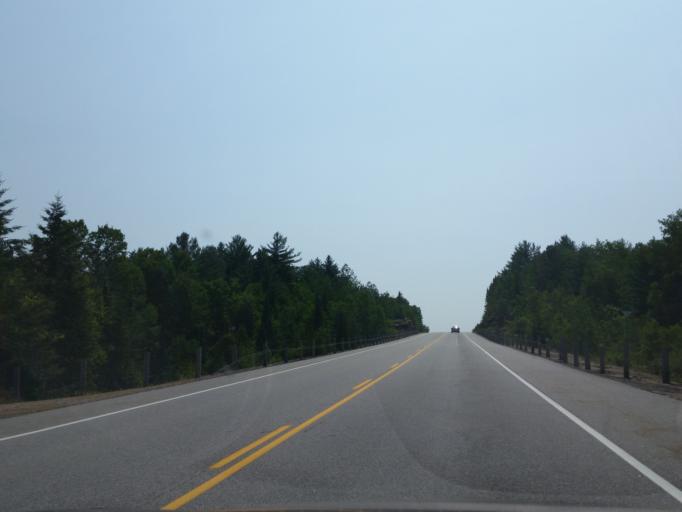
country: CA
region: Ontario
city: Mattawa
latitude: 46.2859
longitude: -78.5129
